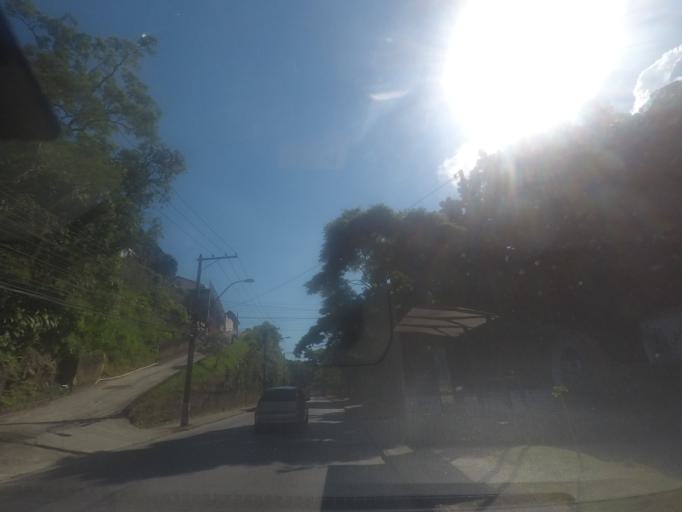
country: BR
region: Rio de Janeiro
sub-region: Petropolis
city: Petropolis
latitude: -22.5311
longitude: -43.1989
